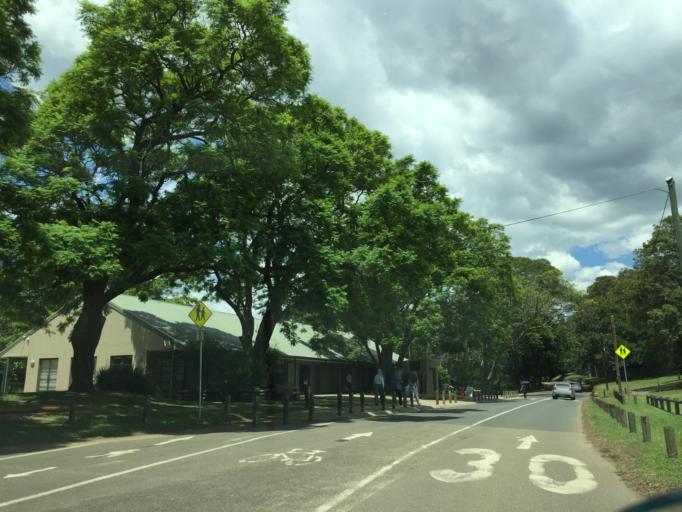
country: AU
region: New South Wales
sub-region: Parramatta
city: City of Parramatta
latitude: -33.8060
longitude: 150.9983
